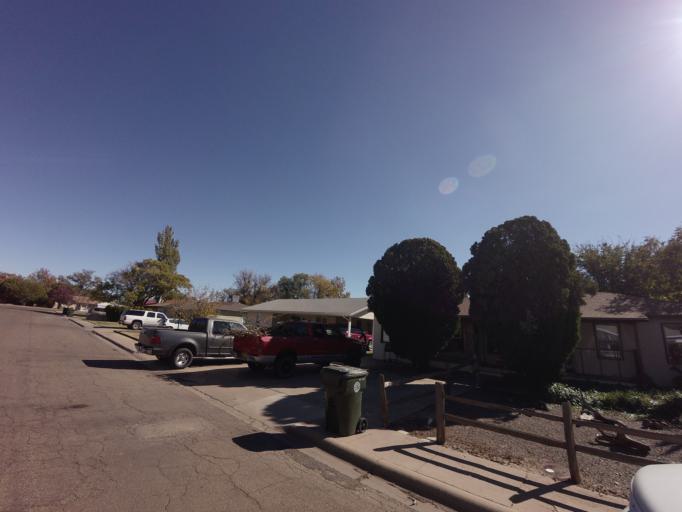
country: US
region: New Mexico
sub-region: Curry County
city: Clovis
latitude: 34.4270
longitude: -103.2037
